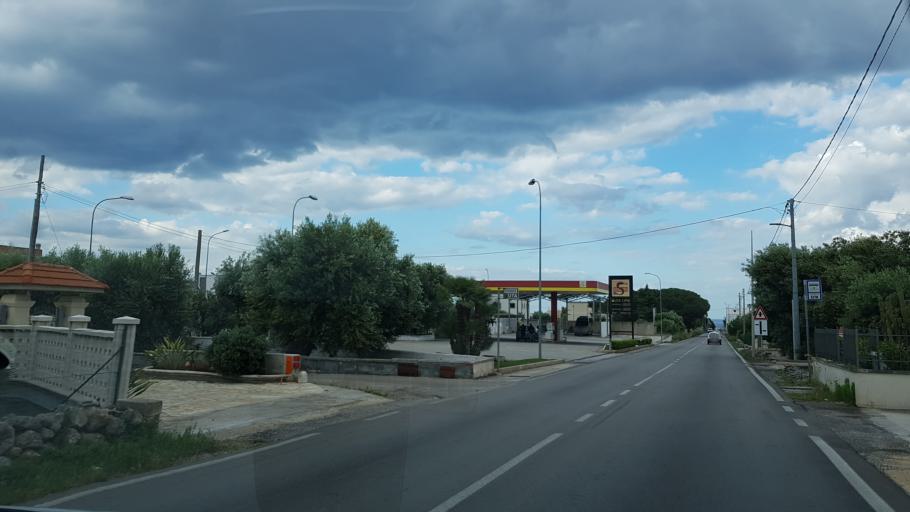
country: IT
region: Apulia
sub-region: Provincia di Brindisi
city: Fasano
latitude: 40.8455
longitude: 17.3804
